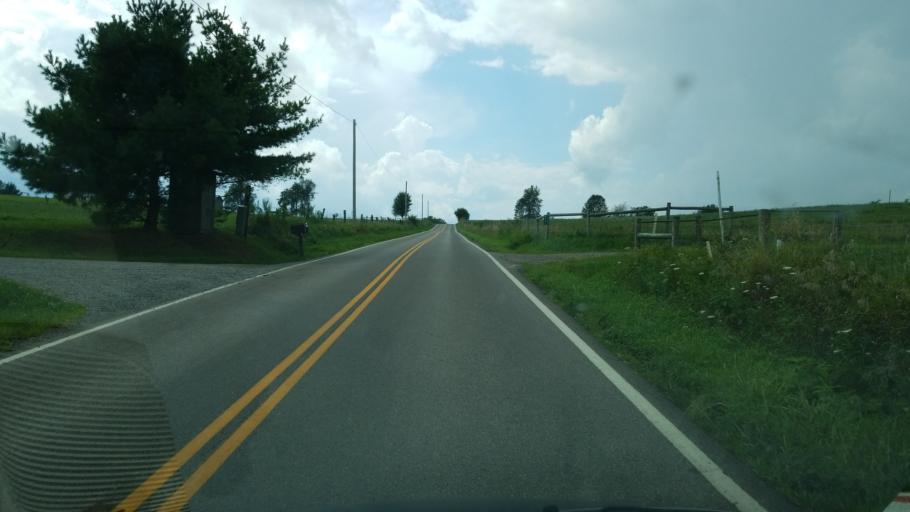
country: US
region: Ohio
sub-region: Tuscarawas County
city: Sugarcreek
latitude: 40.5712
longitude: -81.7589
